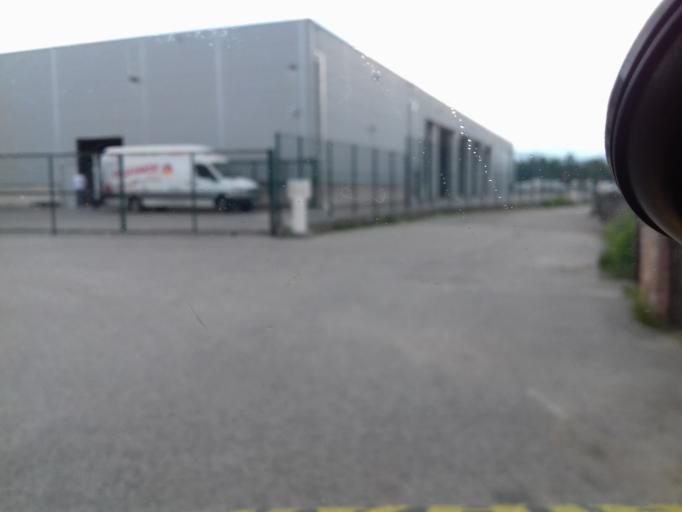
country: BA
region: Federation of Bosnia and Herzegovina
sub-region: Kanton Sarajevo
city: Sarajevo
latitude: 43.8357
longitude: 18.3258
